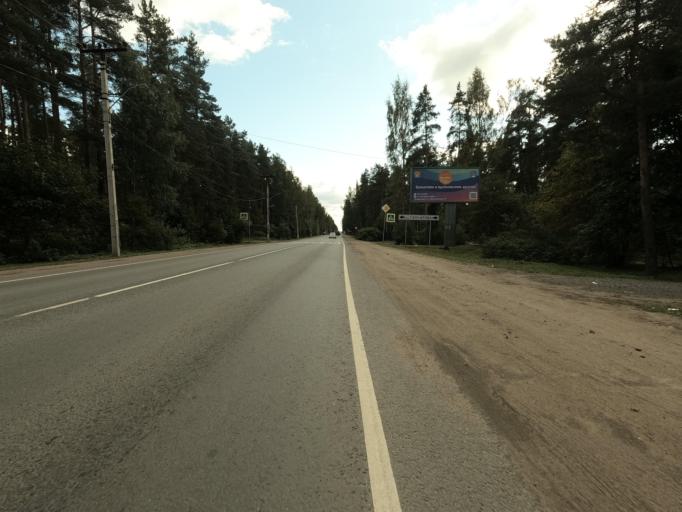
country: RU
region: Leningrad
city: Vsevolozhsk
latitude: 60.0057
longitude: 30.6639
